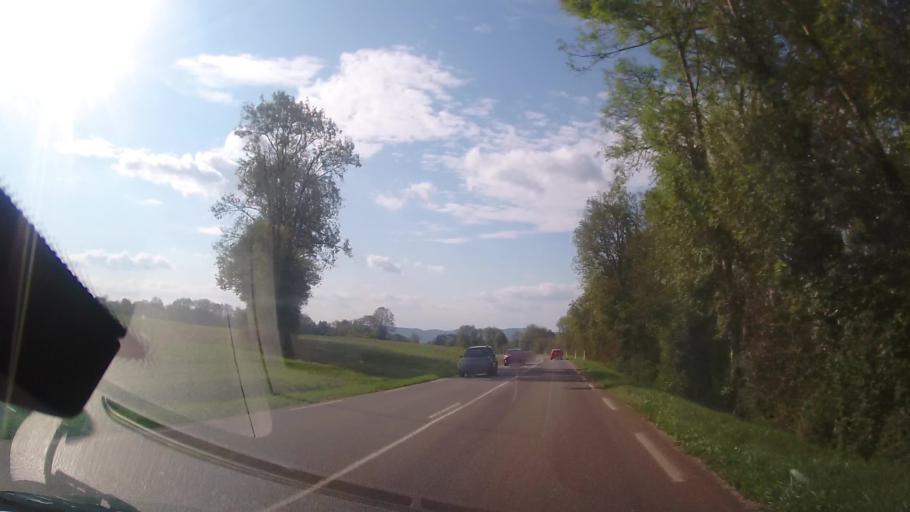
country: FR
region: Franche-Comte
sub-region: Departement du Jura
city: Clairvaux-les-Lacs
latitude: 46.5833
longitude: 5.7707
